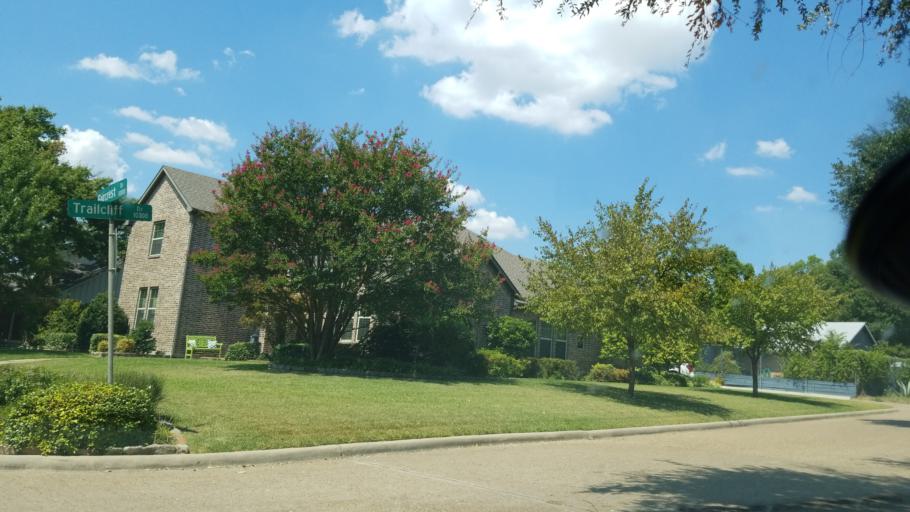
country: US
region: Texas
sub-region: Dallas County
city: Richardson
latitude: 32.8896
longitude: -96.7130
